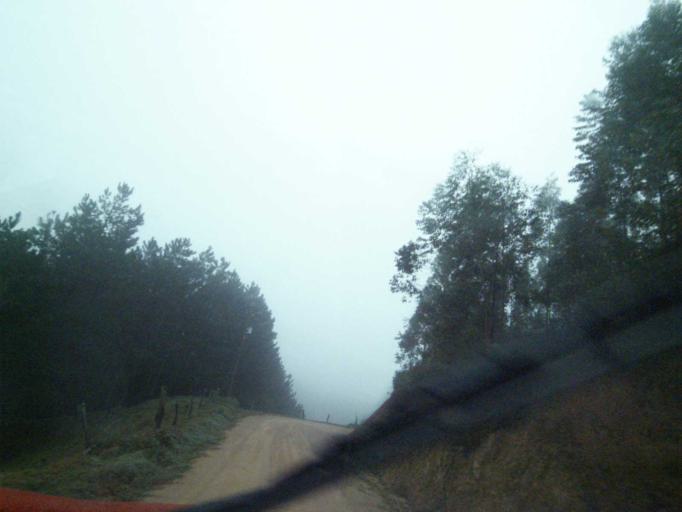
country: BR
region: Santa Catarina
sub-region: Anitapolis
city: Anitapolis
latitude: -27.9129
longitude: -49.0976
